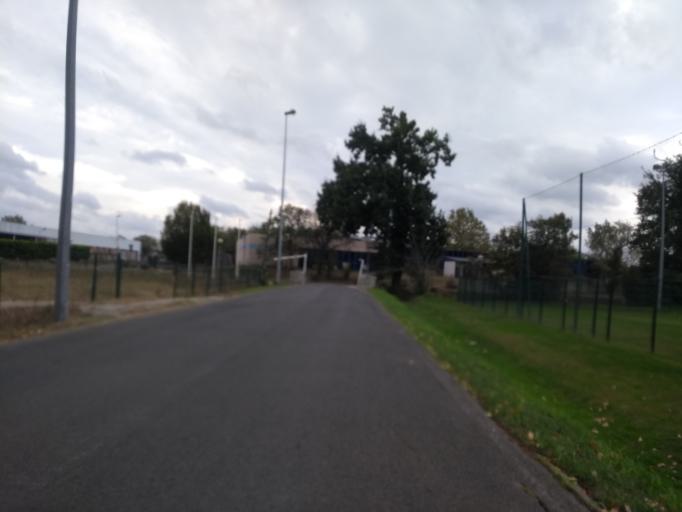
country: FR
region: Aquitaine
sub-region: Departement de la Gironde
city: Talence
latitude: 44.7876
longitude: -0.5933
